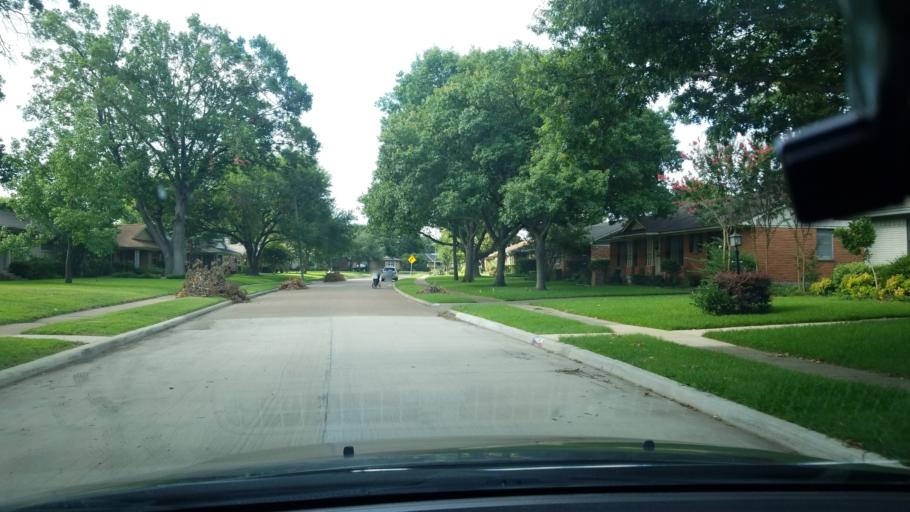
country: US
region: Texas
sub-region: Dallas County
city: Mesquite
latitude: 32.8208
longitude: -96.6857
